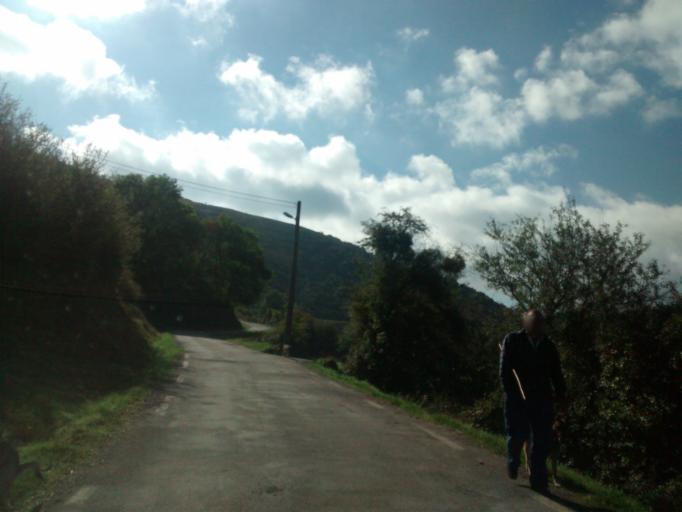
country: ES
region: Castille and Leon
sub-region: Provincia de Burgos
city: Arija
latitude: 42.9349
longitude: -4.0300
